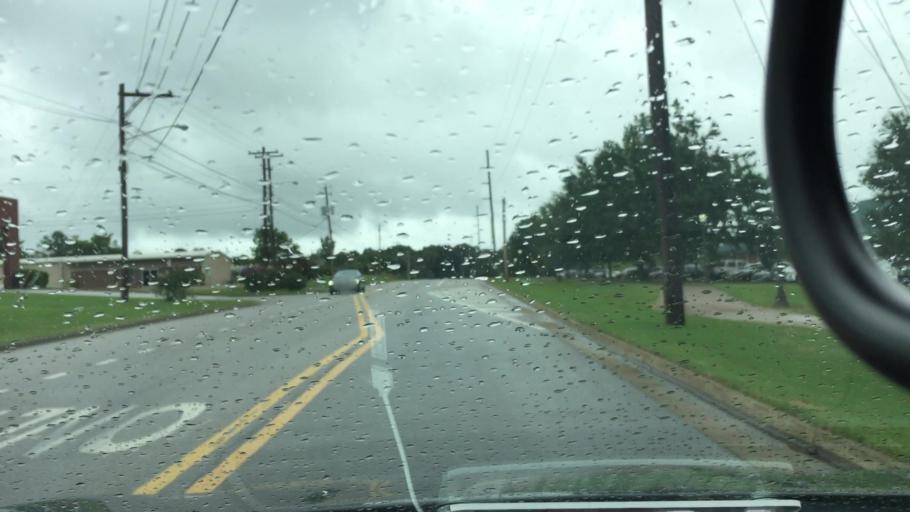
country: US
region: Alabama
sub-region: Lee County
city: Opelika
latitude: 32.6694
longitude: -85.3677
